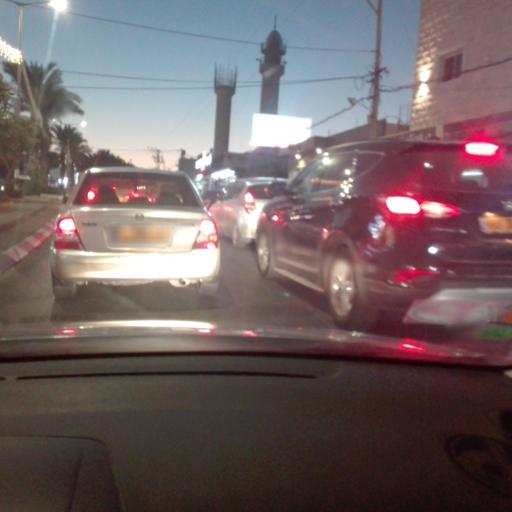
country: PS
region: West Bank
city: Nazlat `Isa
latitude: 32.4204
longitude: 35.0440
